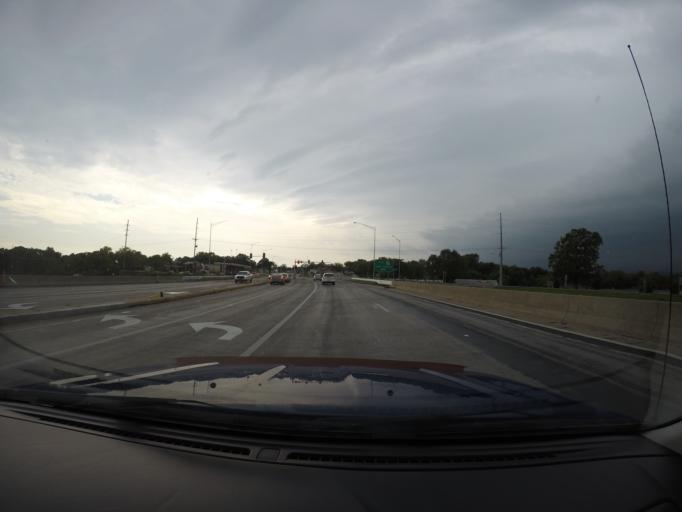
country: US
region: Missouri
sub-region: Jackson County
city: East Independence
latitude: 39.1172
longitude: -94.3848
